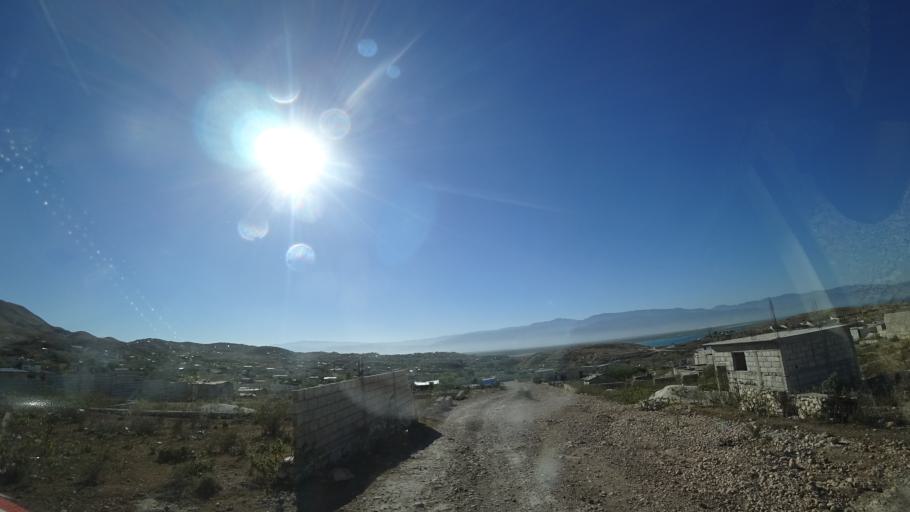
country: HT
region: Ouest
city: Cabaret
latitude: 18.6886
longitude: -72.3176
